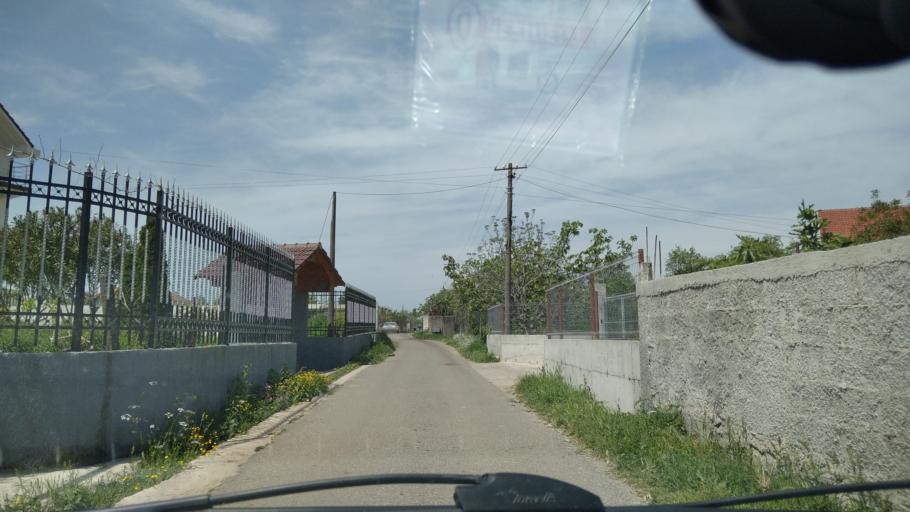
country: AL
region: Shkoder
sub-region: Rrethi i Malesia e Madhe
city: Gruemire
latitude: 42.1467
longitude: 19.5431
